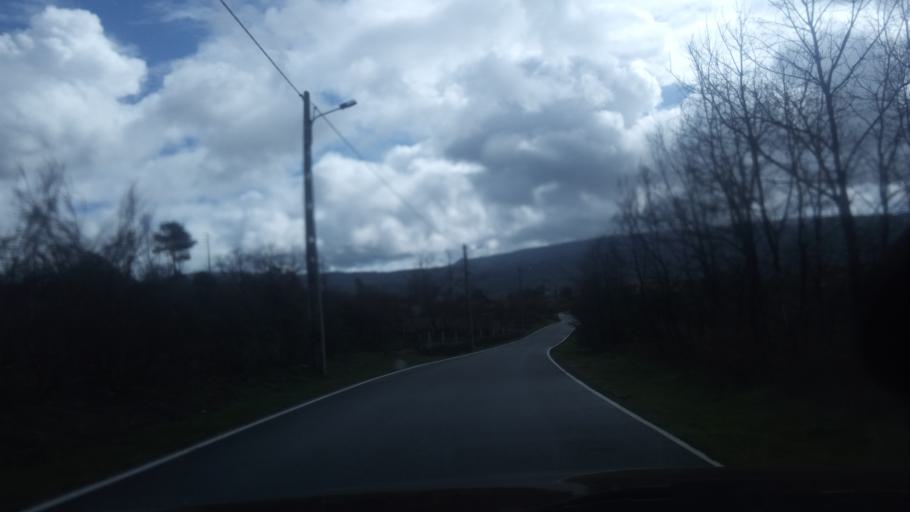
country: PT
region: Guarda
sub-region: Fornos de Algodres
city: Fornos de Algodres
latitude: 40.5851
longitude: -7.4790
